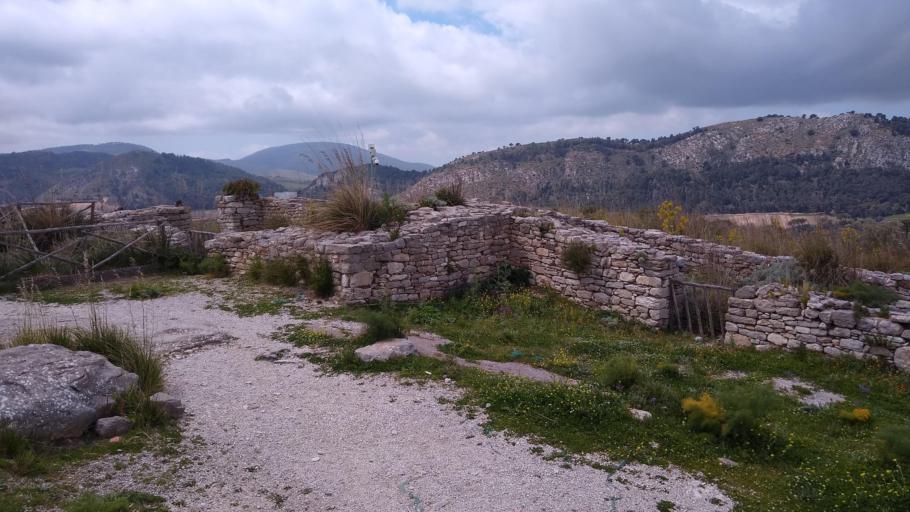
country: IT
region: Sicily
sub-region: Trapani
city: Calatafimi
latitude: 37.9403
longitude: 12.8438
